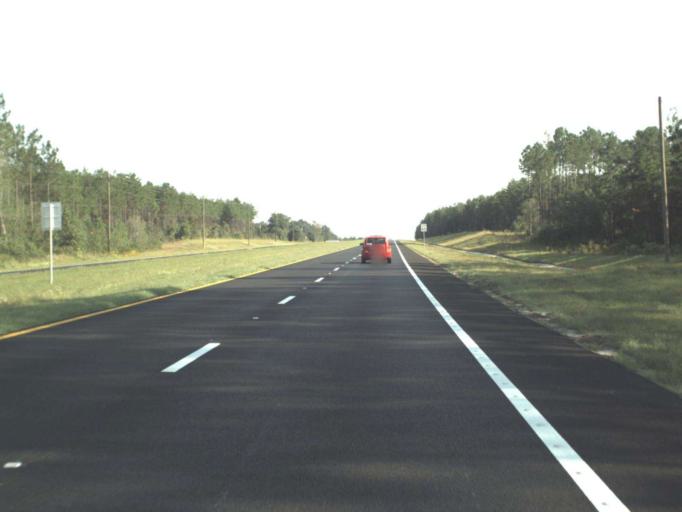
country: US
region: Florida
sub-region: Walton County
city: Freeport
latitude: 30.5302
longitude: -85.8374
